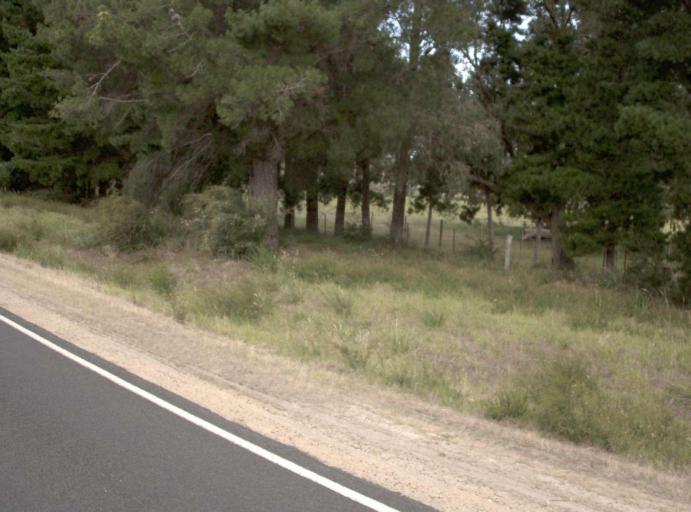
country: AU
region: Victoria
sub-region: Wellington
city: Sale
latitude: -38.2165
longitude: 147.1230
